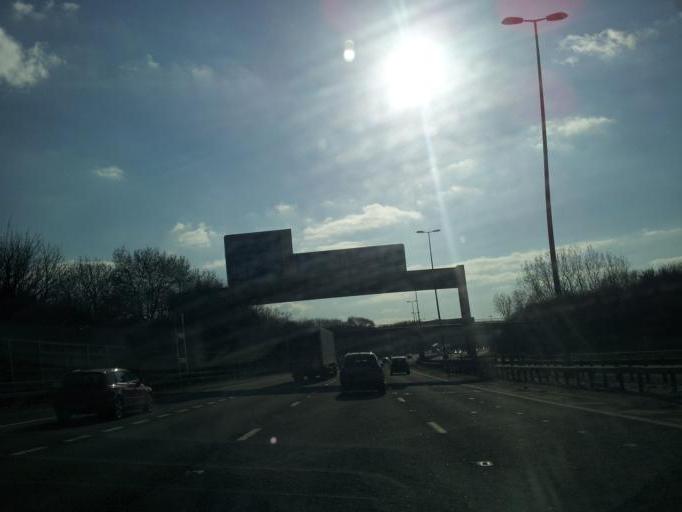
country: GB
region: England
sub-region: North Somerset
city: Easton-in-Gordano
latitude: 51.4804
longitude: -2.7028
